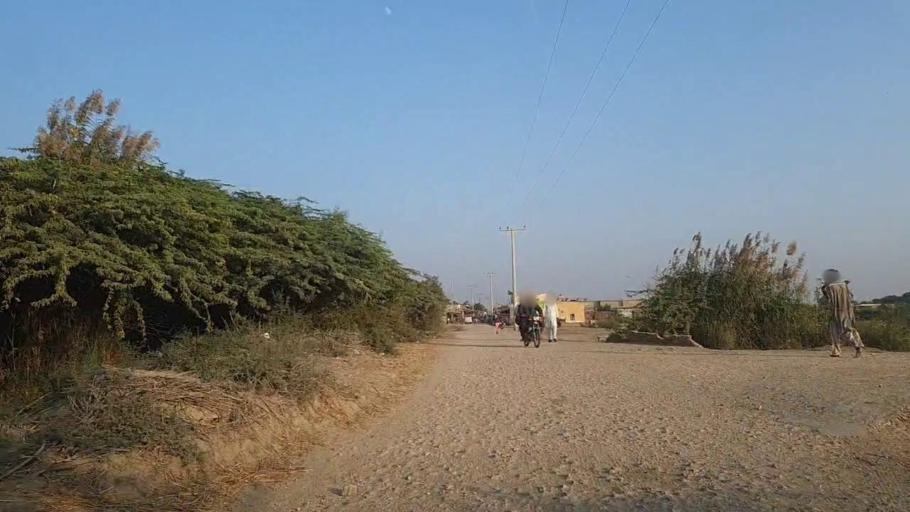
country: PK
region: Sindh
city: Keti Bandar
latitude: 24.2743
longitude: 67.6714
